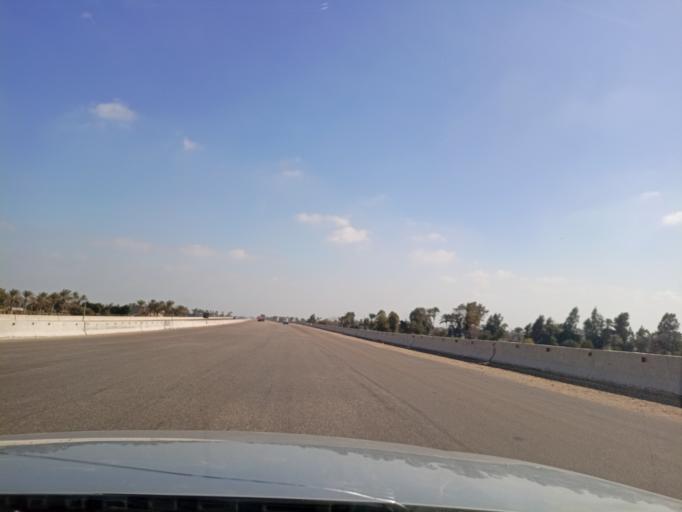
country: EG
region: Eastern Province
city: Mashtul as Suq
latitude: 30.4592
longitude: 31.3453
